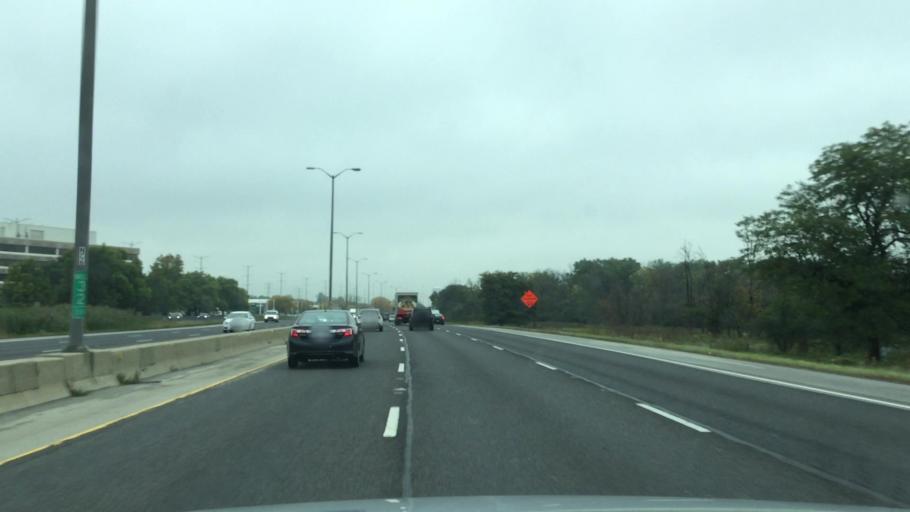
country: US
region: Illinois
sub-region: Cook County
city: Northfield
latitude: 42.1064
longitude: -87.7709
